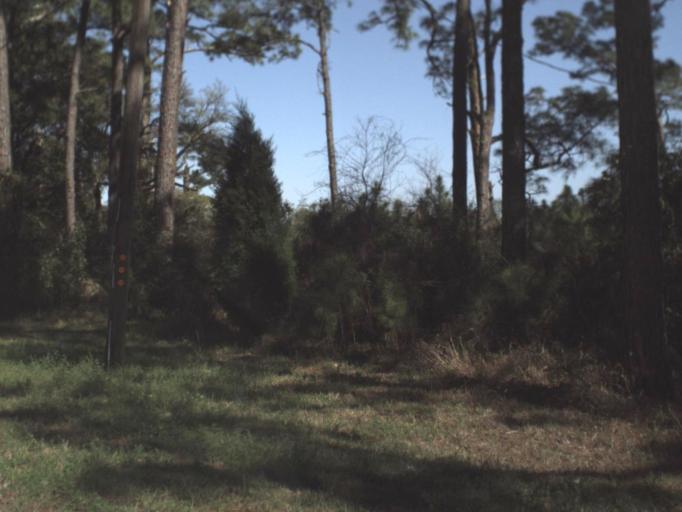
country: US
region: Florida
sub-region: Franklin County
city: Carrabelle
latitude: 29.9001
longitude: -84.5536
